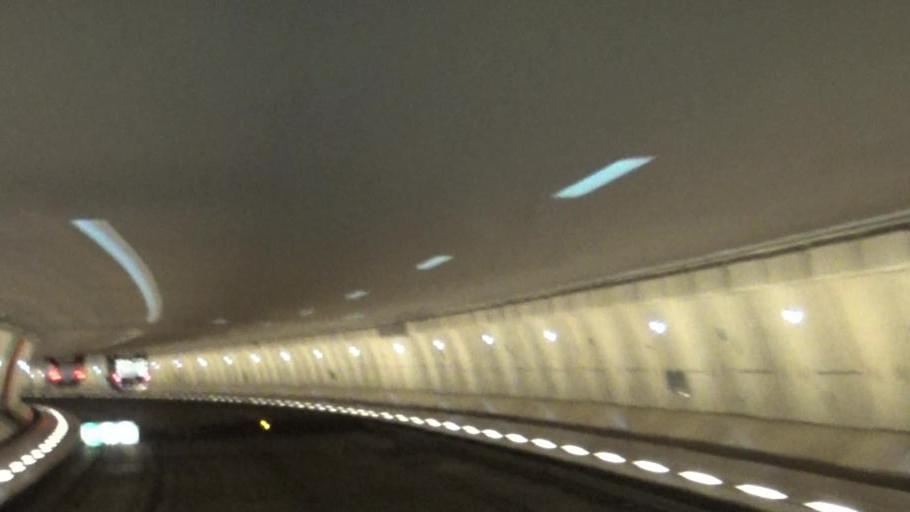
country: FR
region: Ile-de-France
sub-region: Departement des Yvelines
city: La Celle-Saint-Cloud
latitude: 48.8607
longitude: 2.1588
